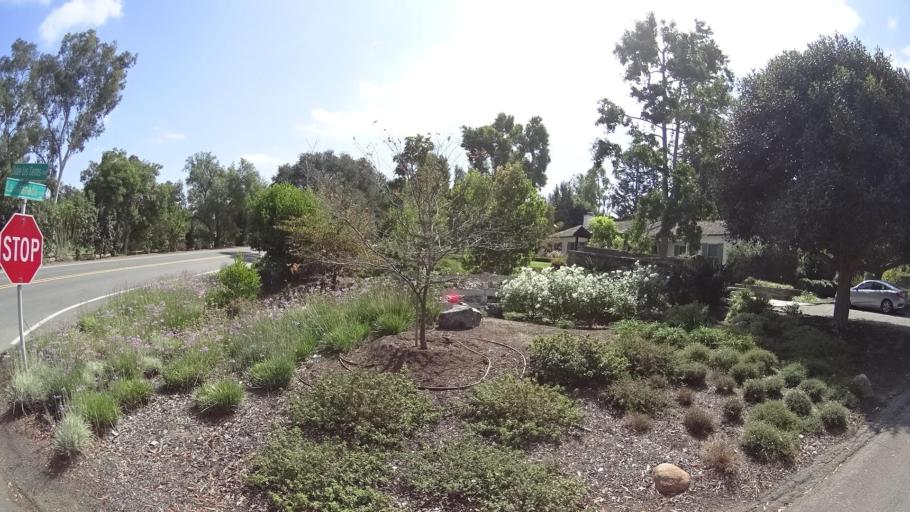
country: US
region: California
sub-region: San Diego County
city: Rancho Santa Fe
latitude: 33.0229
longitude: -117.2133
